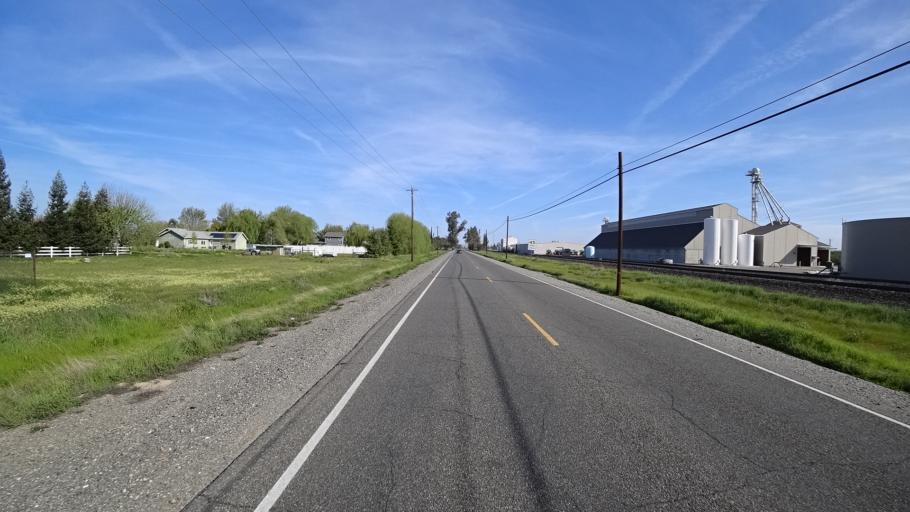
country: US
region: California
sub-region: Glenn County
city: Willows
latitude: 39.6131
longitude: -122.1942
